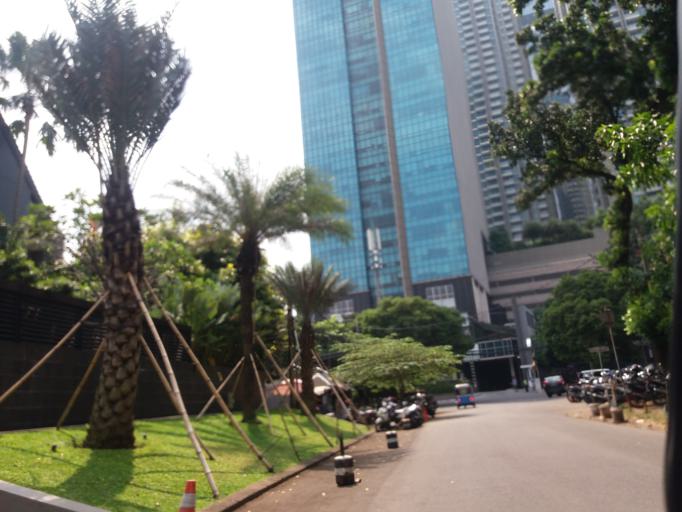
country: ID
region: Jakarta Raya
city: Jakarta
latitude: -6.2306
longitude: 106.8058
